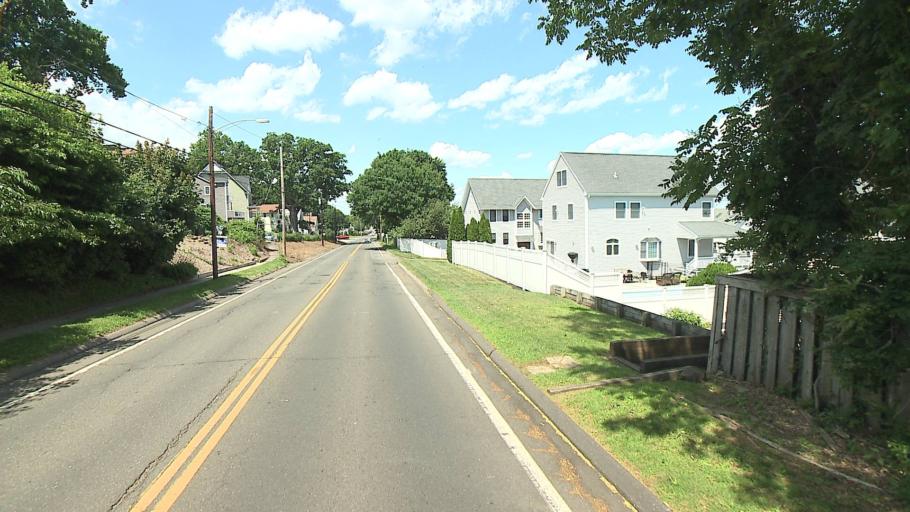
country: US
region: Connecticut
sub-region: New Haven County
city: Woodmont
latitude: 41.2185
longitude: -73.0066
